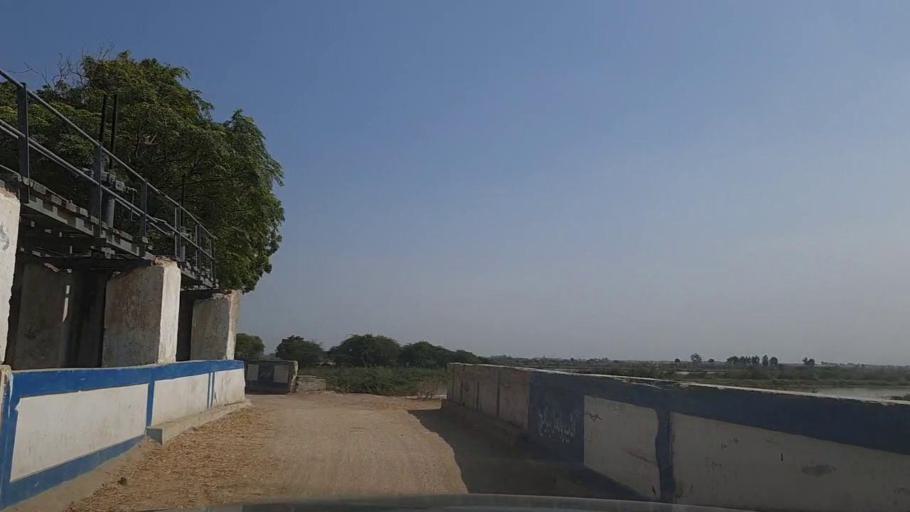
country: PK
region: Sindh
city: Thatta
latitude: 24.5797
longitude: 67.8992
